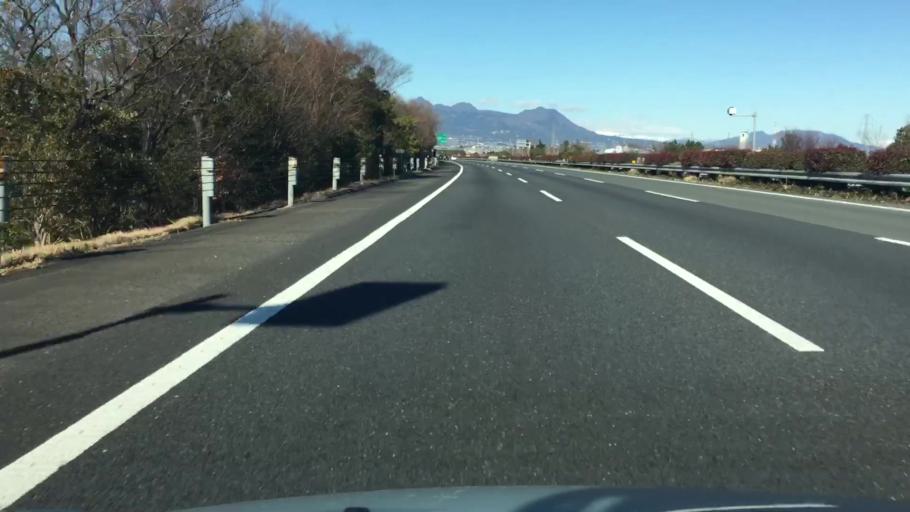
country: JP
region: Gunma
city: Takasaki
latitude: 36.3448
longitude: 139.0535
